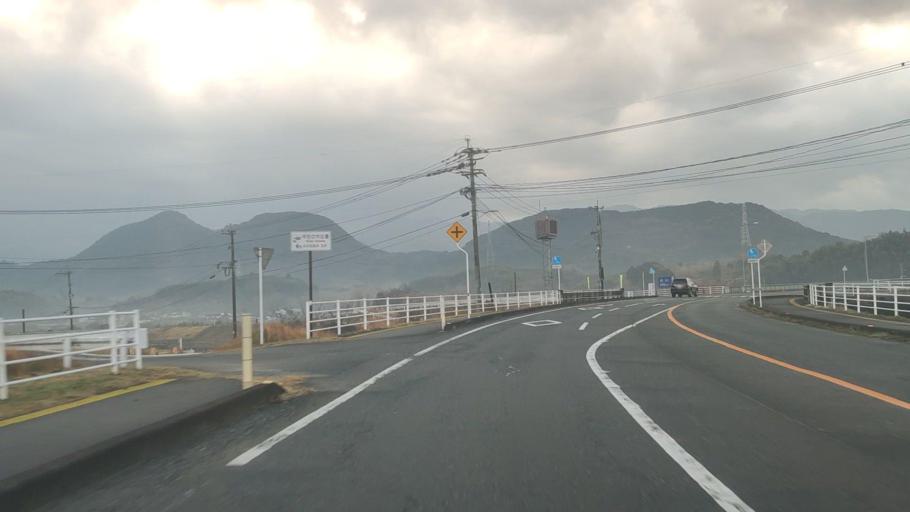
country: JP
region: Kumamoto
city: Matsubase
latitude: 32.6439
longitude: 130.8127
